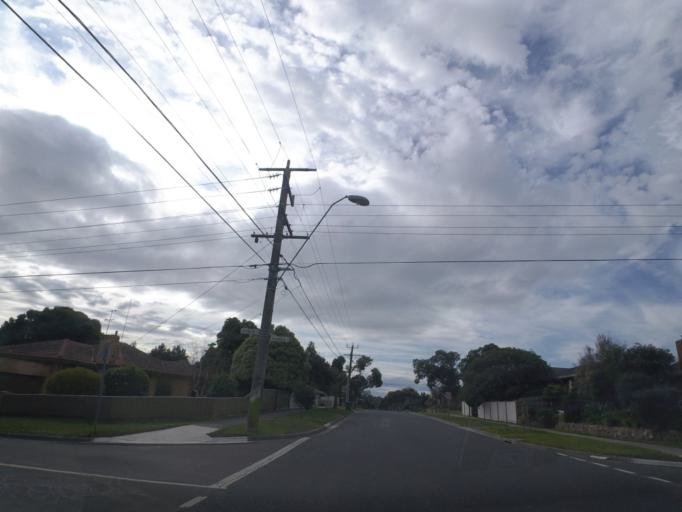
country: AU
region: Victoria
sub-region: Maroondah
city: Heathmont
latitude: -37.8298
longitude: 145.2373
